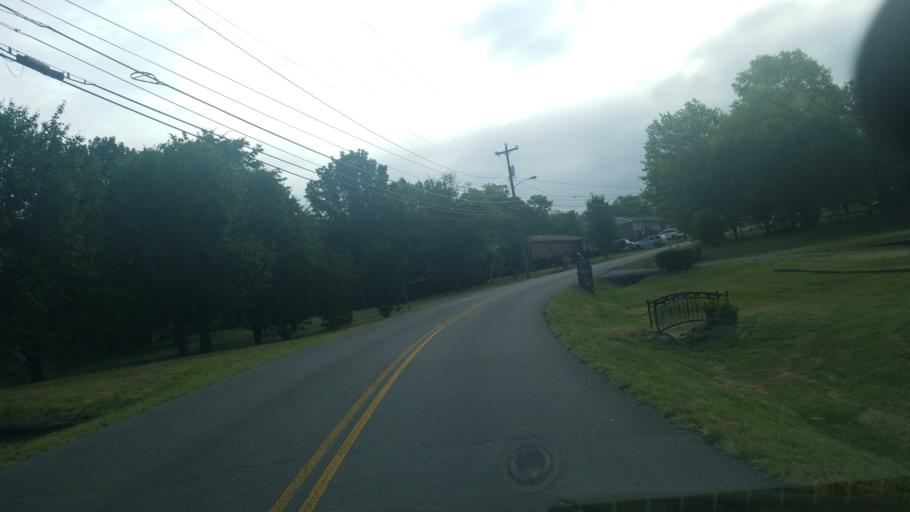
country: US
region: Tennessee
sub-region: Davidson County
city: Nashville
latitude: 36.2364
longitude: -86.7499
